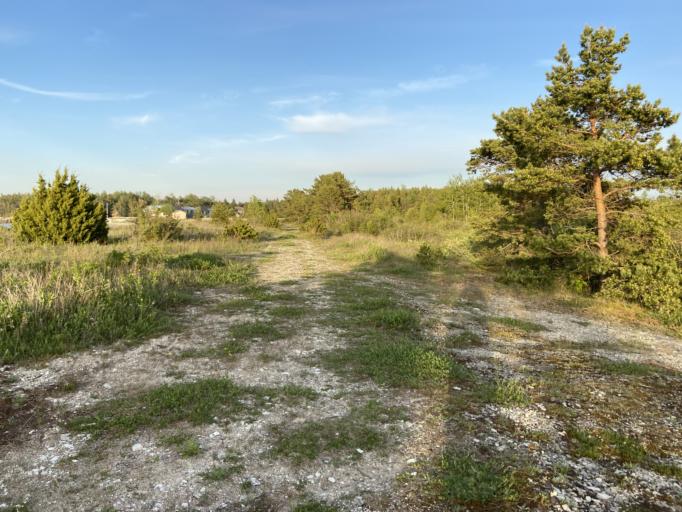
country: EE
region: Harju
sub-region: Paldiski linn
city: Paldiski
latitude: 59.2701
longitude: 23.7397
